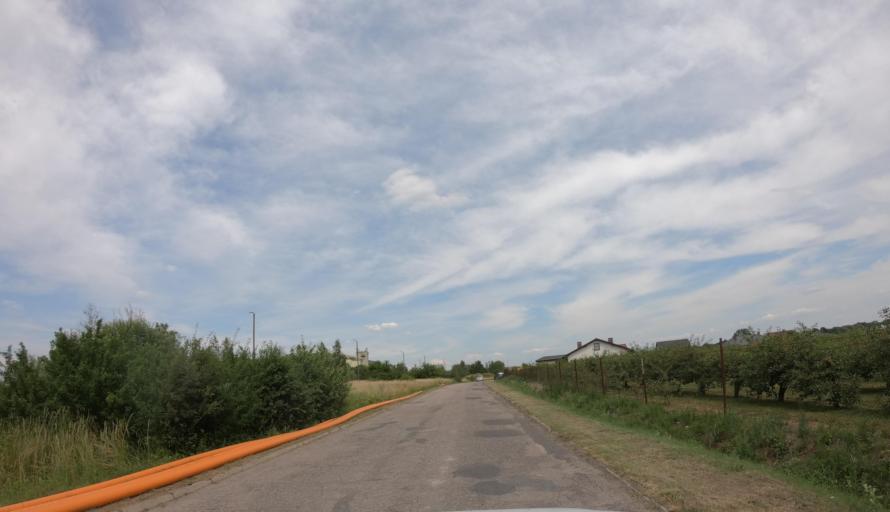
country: PL
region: West Pomeranian Voivodeship
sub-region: Powiat pyrzycki
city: Pyrzyce
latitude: 53.1428
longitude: 14.8750
